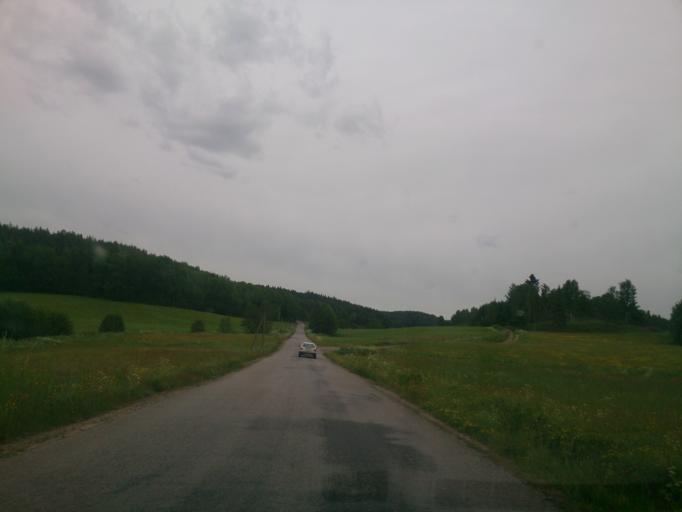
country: SE
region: OEstergoetland
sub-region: Soderkopings Kommun
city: Soederkoeping
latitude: 58.3180
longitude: 16.3047
